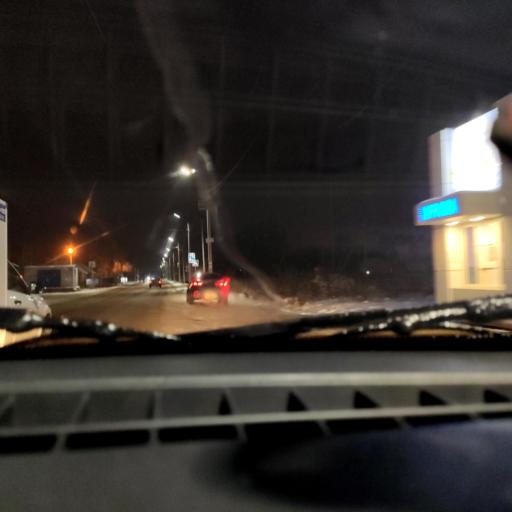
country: RU
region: Bashkortostan
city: Ufa
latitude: 54.6632
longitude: 56.0724
